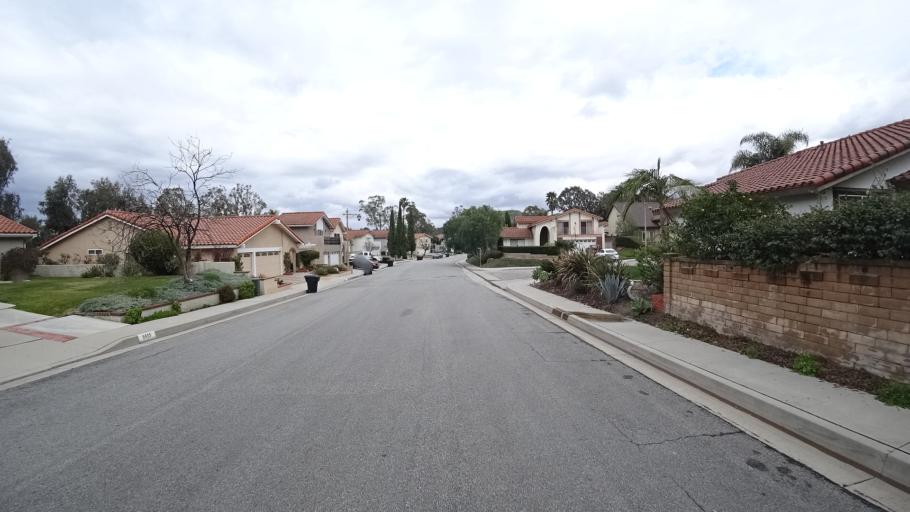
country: US
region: California
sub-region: Orange County
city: Villa Park
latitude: 33.8348
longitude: -117.7523
